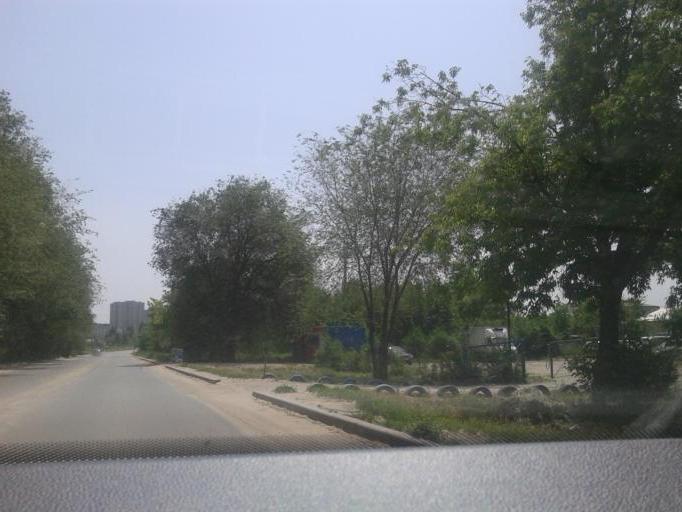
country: RU
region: Volgograd
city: Gorodishche
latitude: 48.7662
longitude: 44.4975
